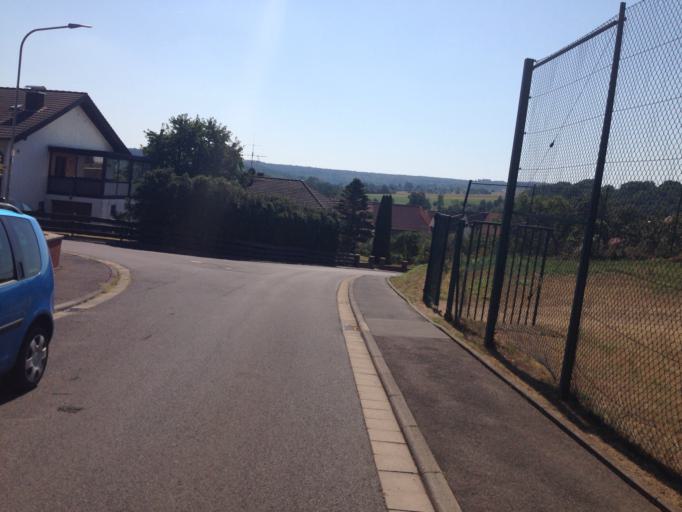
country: DE
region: Hesse
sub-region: Regierungsbezirk Giessen
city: Schoeffengrund
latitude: 50.5046
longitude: 8.5421
